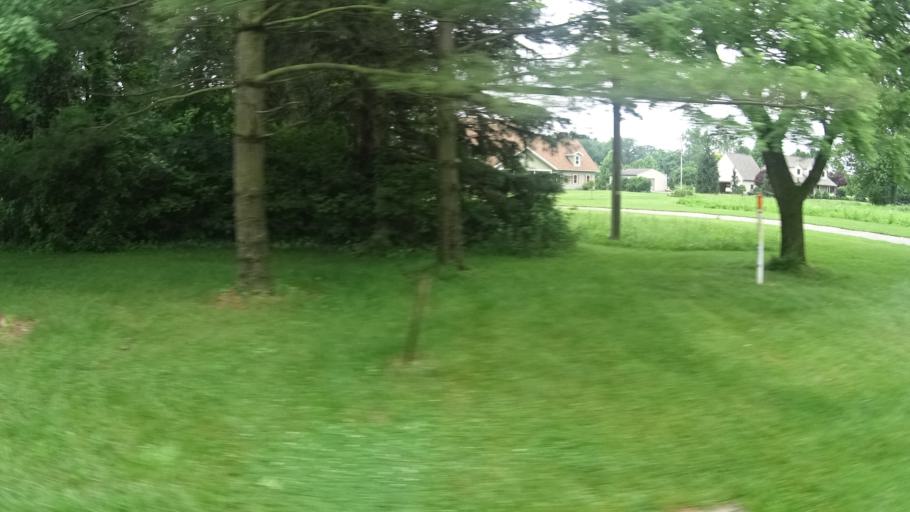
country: US
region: Ohio
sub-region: Erie County
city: Huron
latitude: 41.3432
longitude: -82.5592
